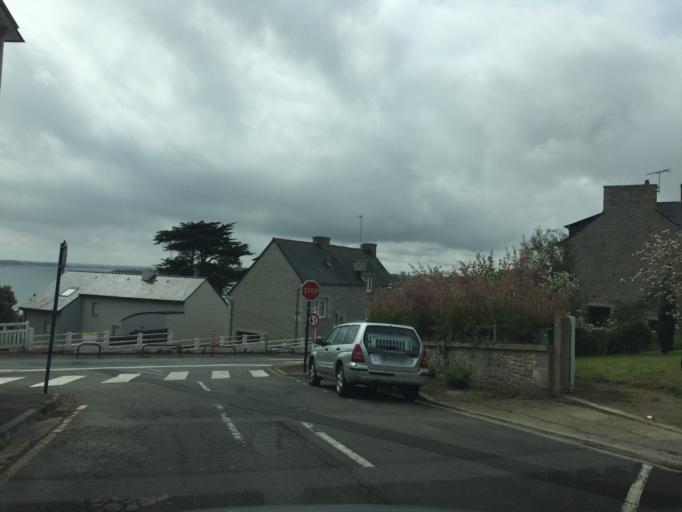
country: FR
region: Brittany
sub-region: Departement des Cotes-d'Armor
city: Saint-Cast-le-Guildo
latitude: 48.6382
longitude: -2.2549
